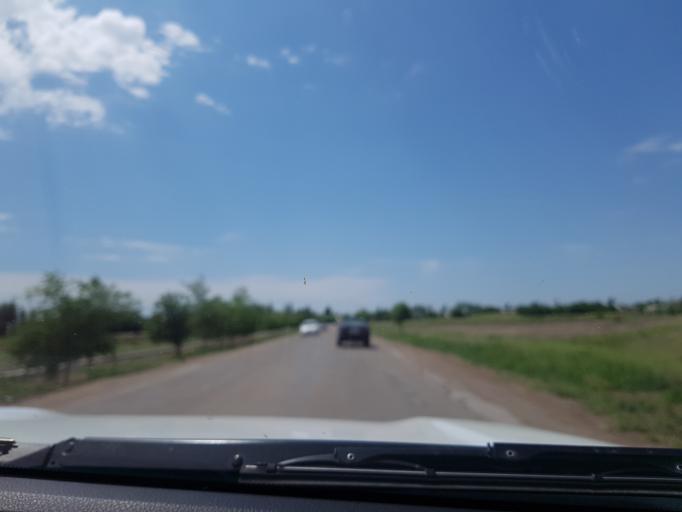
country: TM
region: Dasoguz
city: Koeneuergench
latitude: 42.3199
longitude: 59.1397
